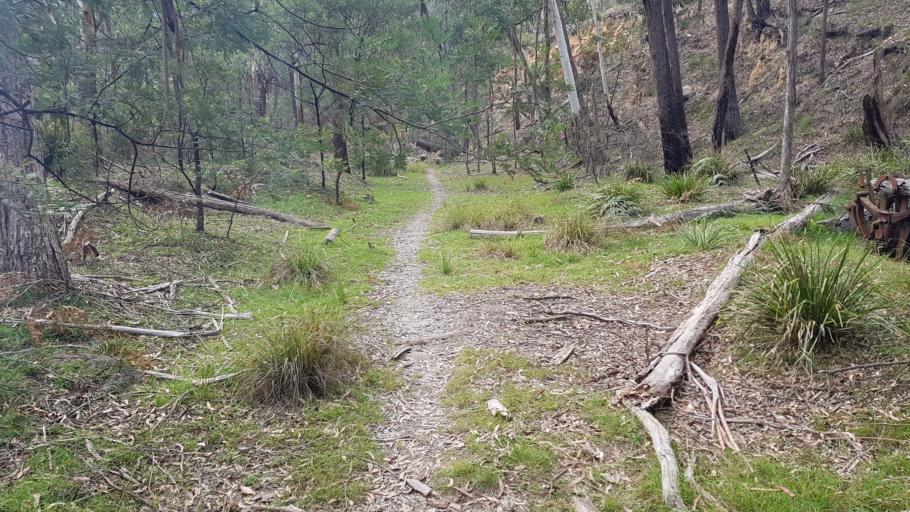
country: AU
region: New South Wales
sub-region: Lithgow
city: Lithgow
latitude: -33.2009
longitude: 150.2454
